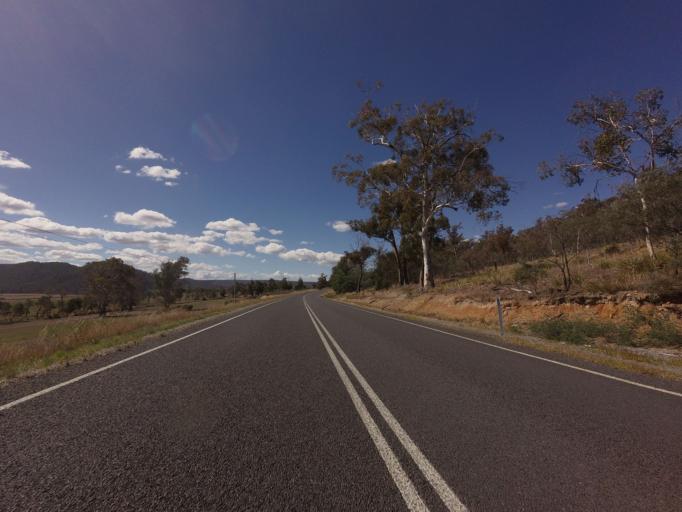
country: AU
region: Tasmania
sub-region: Break O'Day
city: St Helens
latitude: -41.6854
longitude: 147.8819
